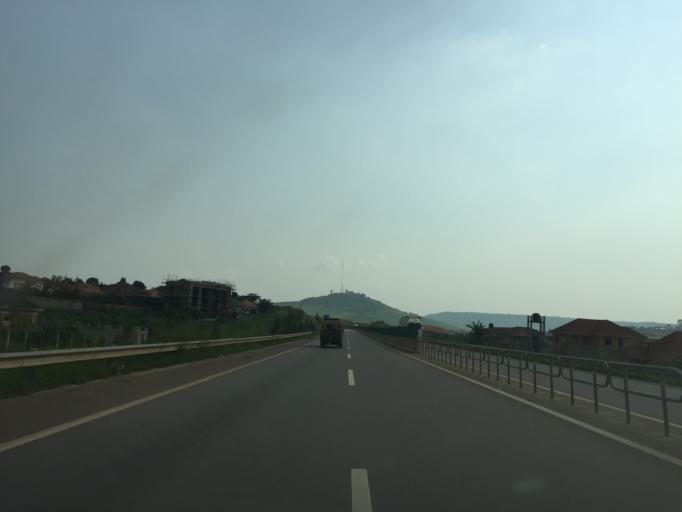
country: UG
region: Central Region
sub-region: Wakiso District
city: Kajansi
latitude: 0.2372
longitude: 32.5239
